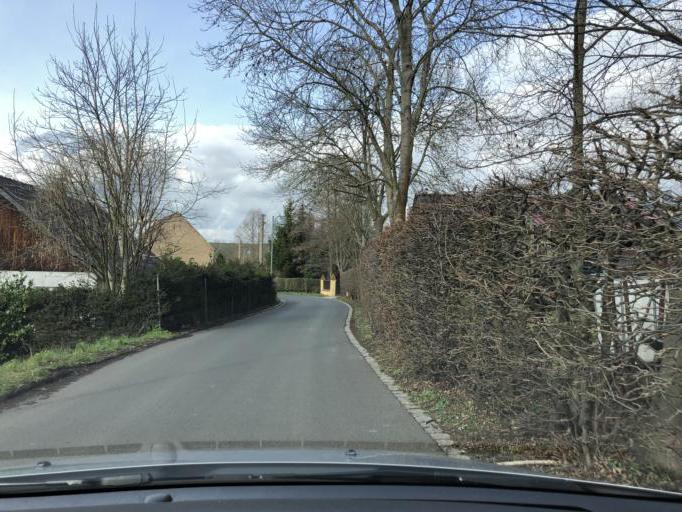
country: DE
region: Saxony
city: Ostrau
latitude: 51.2058
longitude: 12.8859
